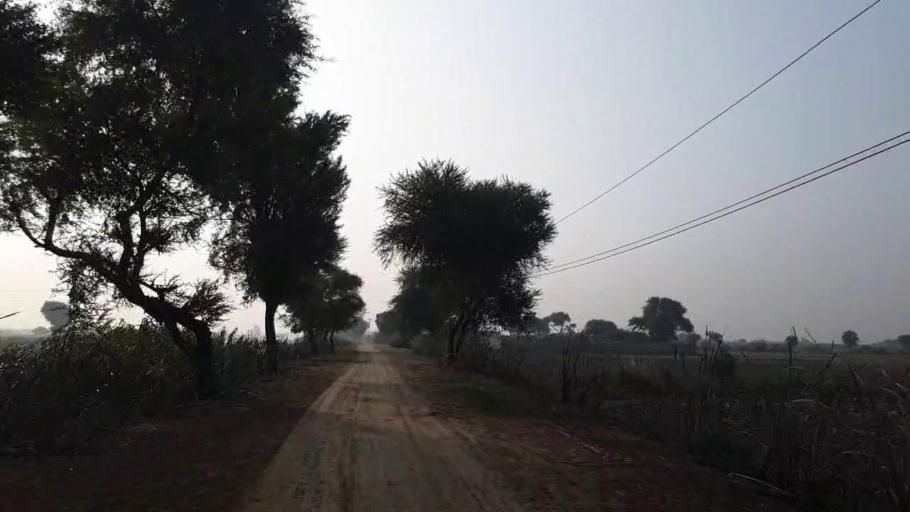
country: PK
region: Sindh
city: Tando Muhammad Khan
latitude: 25.1087
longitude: 68.5702
